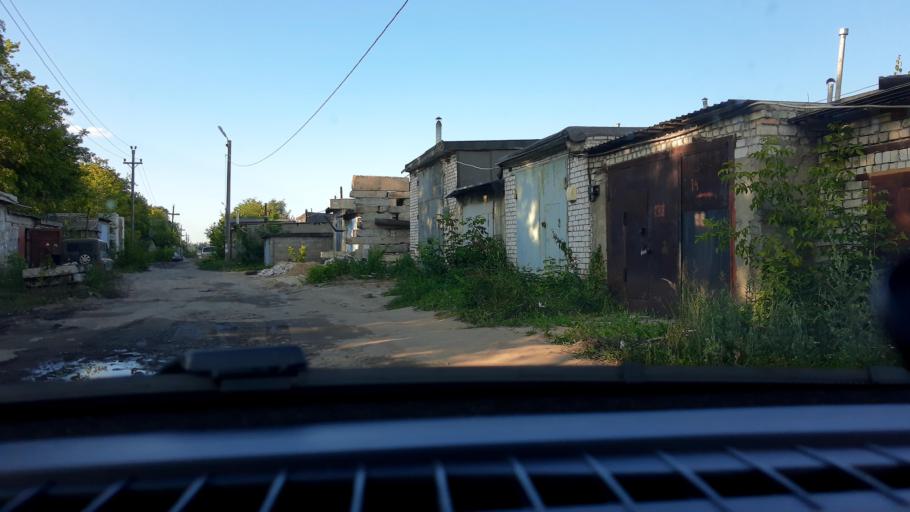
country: RU
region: Nizjnij Novgorod
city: Gorbatovka
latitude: 56.2493
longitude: 43.8241
